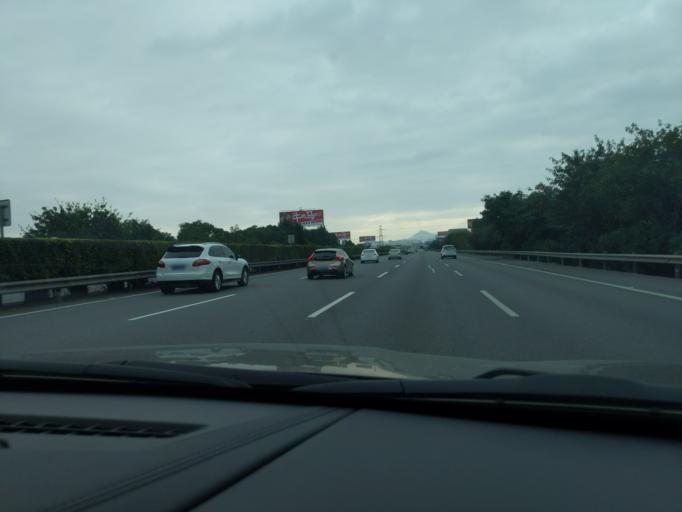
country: CN
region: Fujian
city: Neikeng
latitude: 24.7690
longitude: 118.4523
